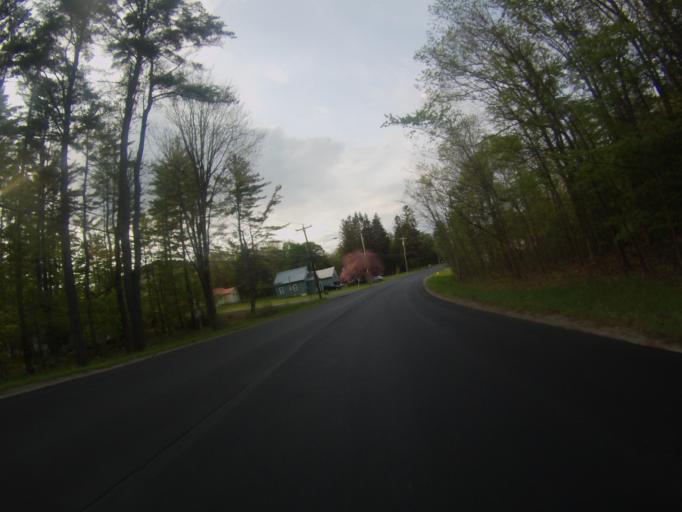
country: US
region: New York
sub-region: Essex County
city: Ticonderoga
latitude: 43.8094
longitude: -73.4887
